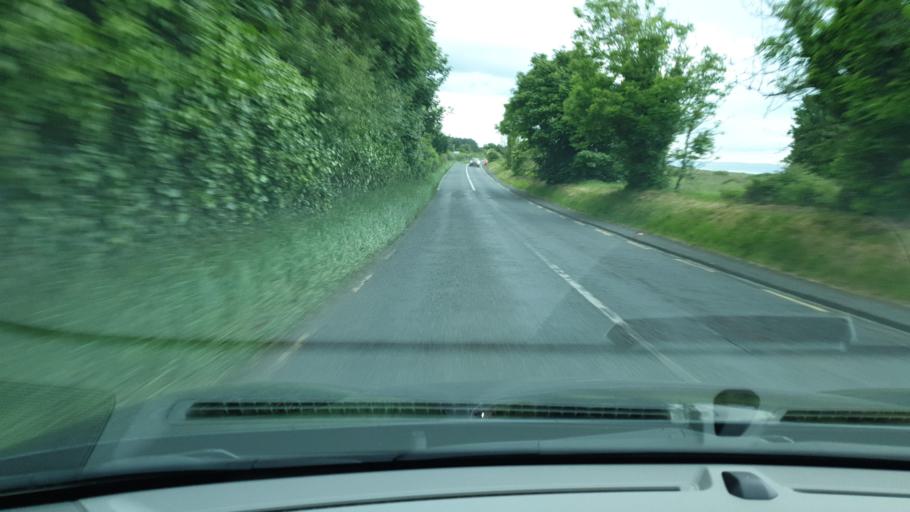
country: IE
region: Leinster
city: Balrothery
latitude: 53.5927
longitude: -6.1576
